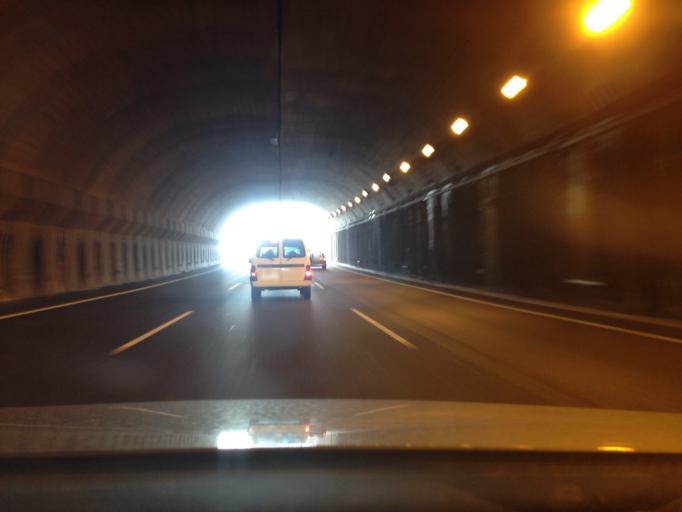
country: ES
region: Canary Islands
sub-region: Provincia de Santa Cruz de Tenerife
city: La Laguna
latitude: 28.4811
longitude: -16.3186
